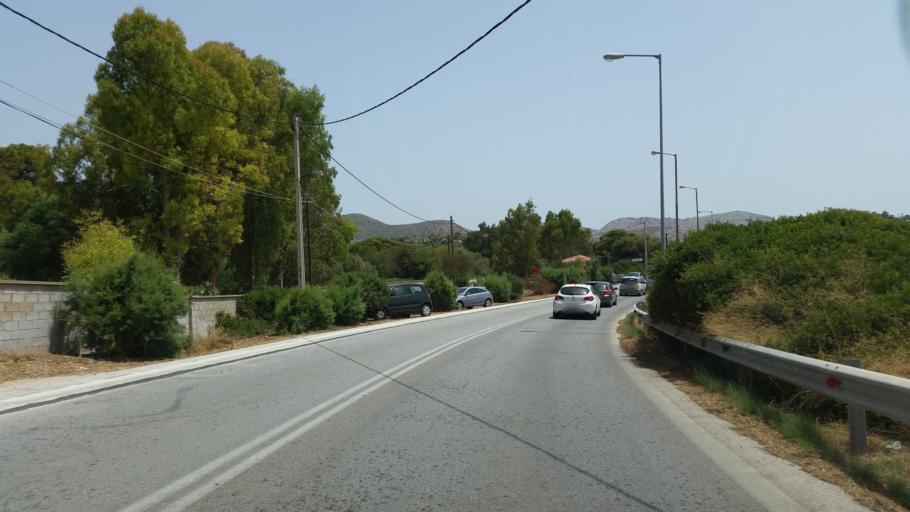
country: GR
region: Attica
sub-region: Nomarchia Anatolikis Attikis
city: Palaia Fokaia
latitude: 37.7043
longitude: 23.9398
